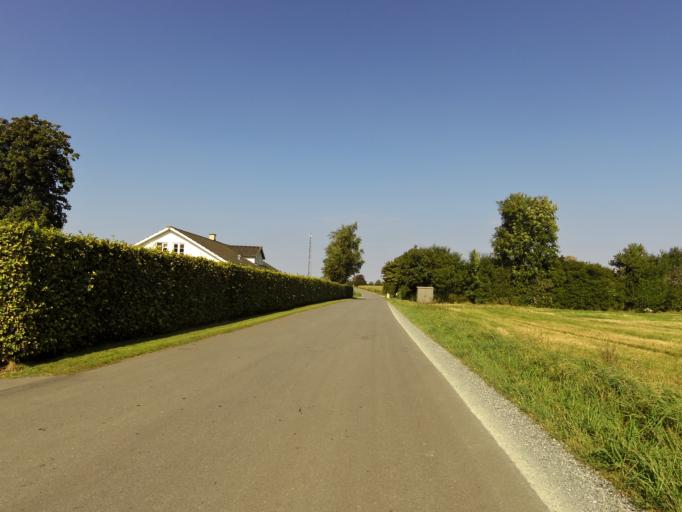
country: DK
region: South Denmark
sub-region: Vejen Kommune
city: Rodding
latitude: 55.3551
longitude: 9.1270
